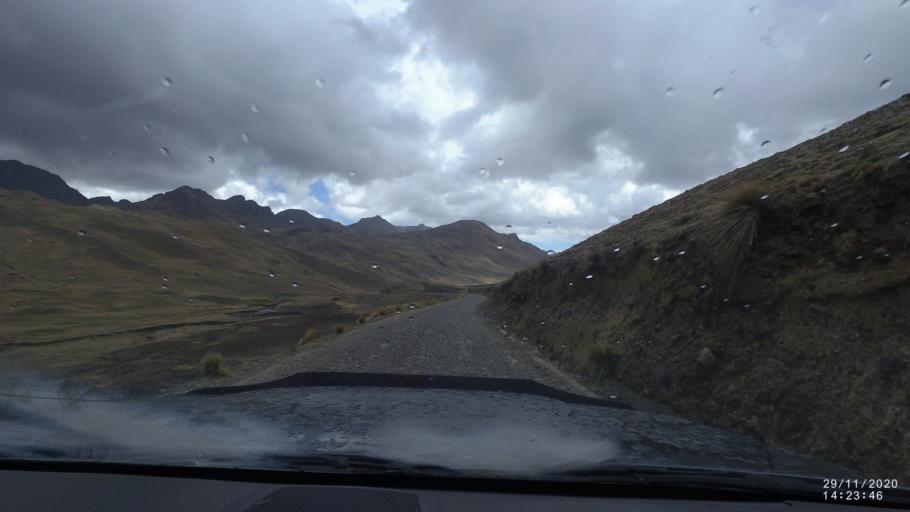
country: BO
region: Cochabamba
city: Sipe Sipe
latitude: -17.2549
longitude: -66.3827
